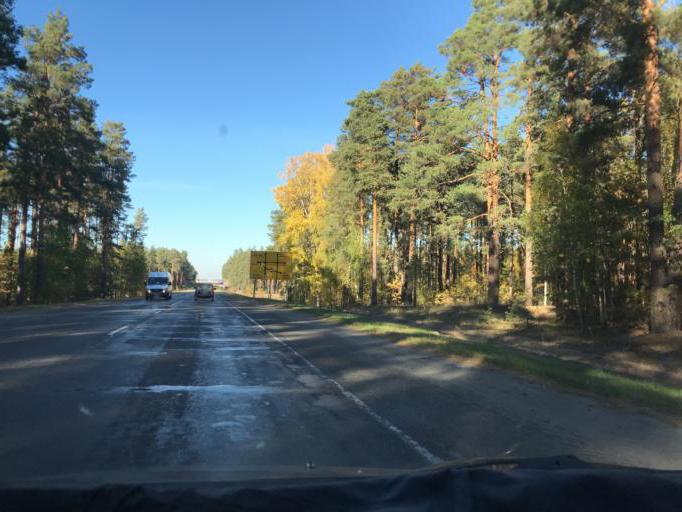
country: BY
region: Gomel
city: Kalinkavichy
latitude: 52.0625
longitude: 29.3610
